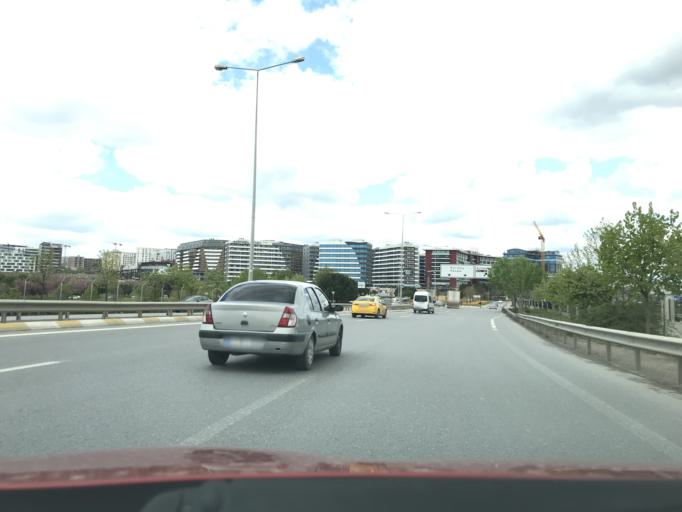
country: TR
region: Istanbul
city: Sultanbeyli
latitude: 40.9226
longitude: 29.3128
